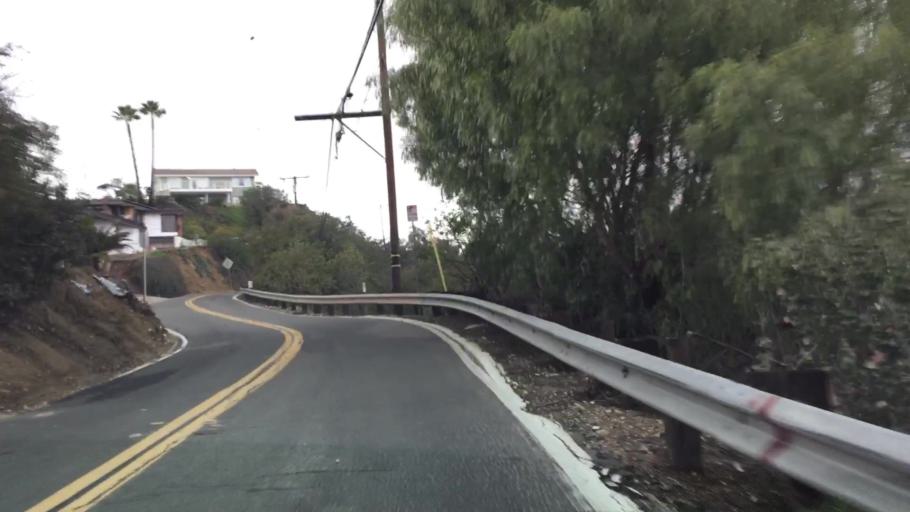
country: US
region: California
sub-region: Los Angeles County
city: Hacienda Heights
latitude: 33.9939
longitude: -117.9964
